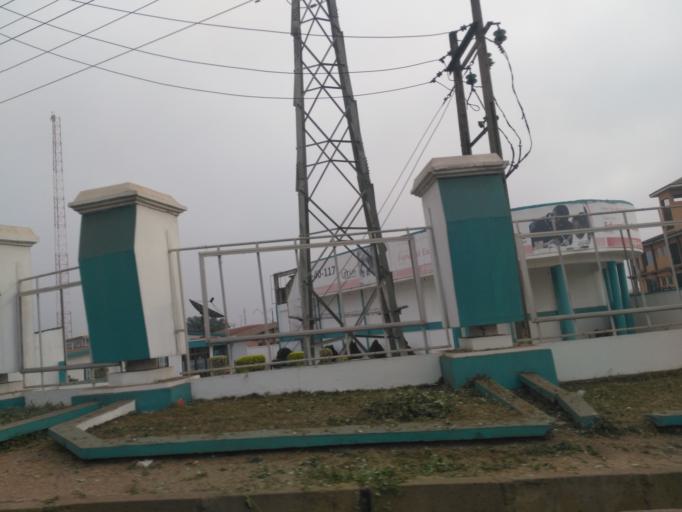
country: GH
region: Ashanti
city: Tafo
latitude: 6.7140
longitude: -1.6032
